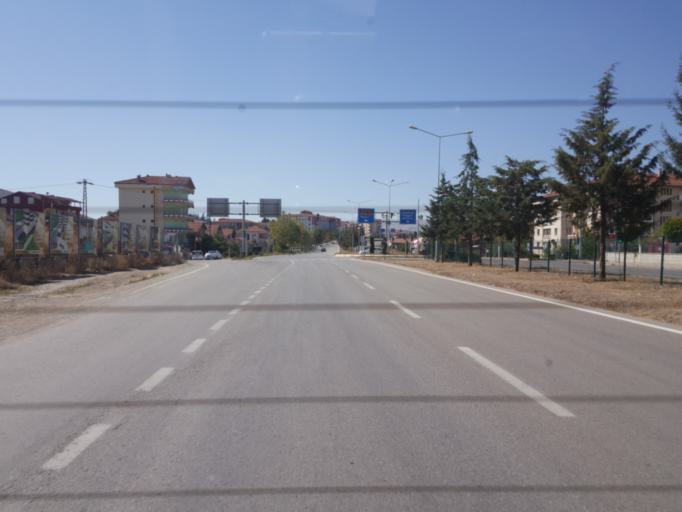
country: TR
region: Tokat
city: Zile
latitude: 40.2974
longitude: 35.8938
